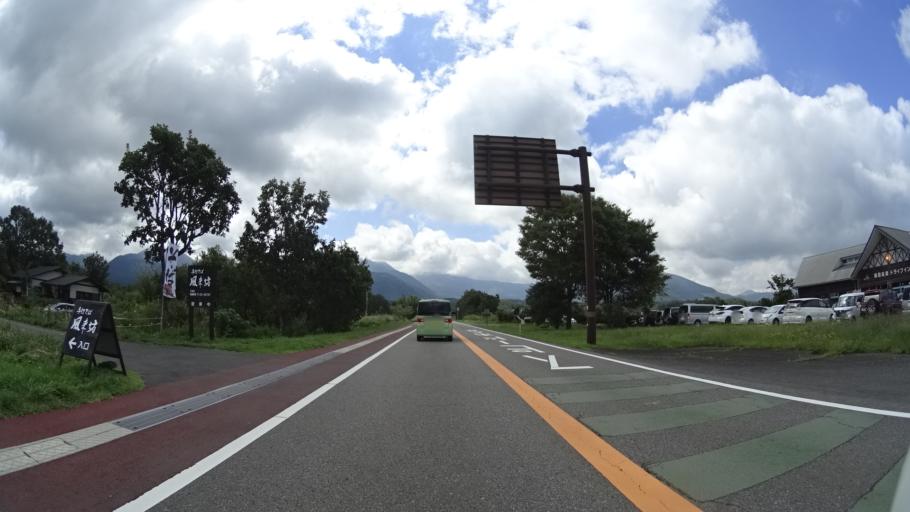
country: JP
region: Oita
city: Tsukawaki
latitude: 33.1563
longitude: 131.2411
